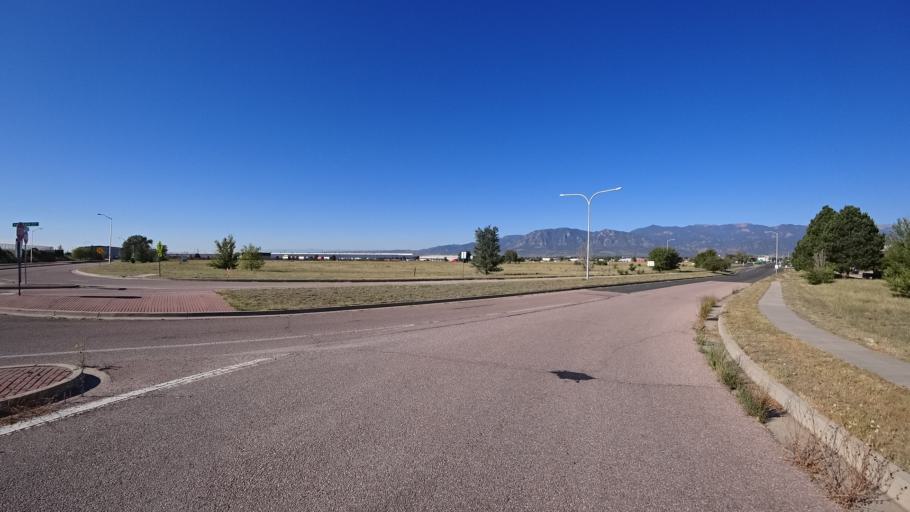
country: US
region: Colorado
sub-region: El Paso County
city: Cimarron Hills
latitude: 38.8063
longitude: -104.7240
